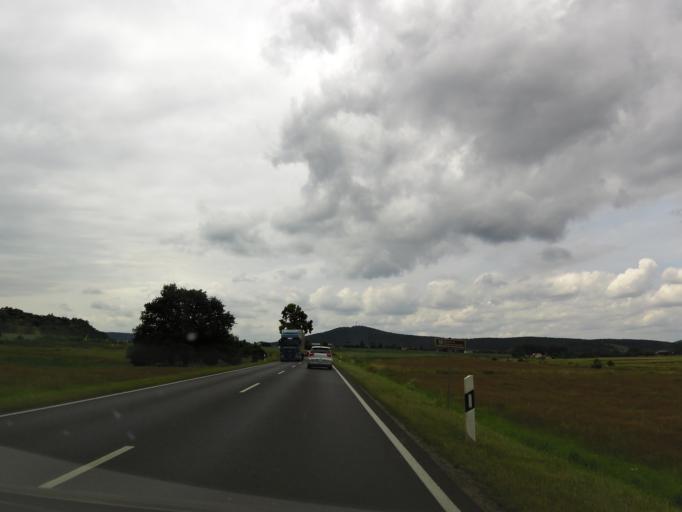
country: DE
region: Thuringia
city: Tiefenort
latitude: 50.8229
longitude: 10.1757
